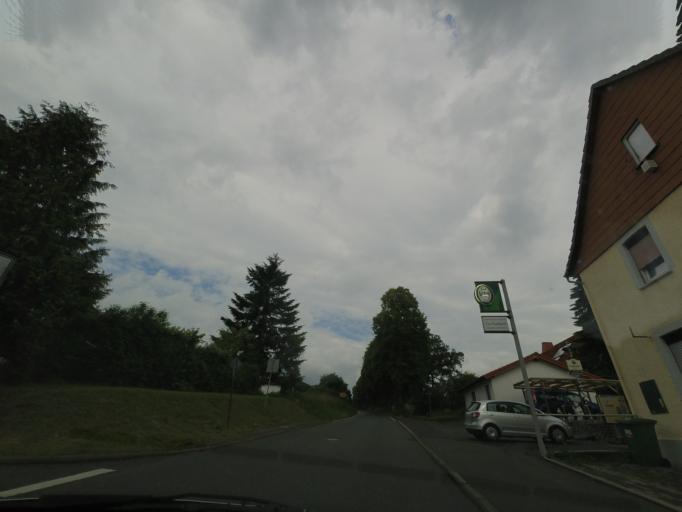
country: DE
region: Hesse
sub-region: Regierungsbezirk Giessen
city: Lohra
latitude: 50.6684
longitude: 8.5964
